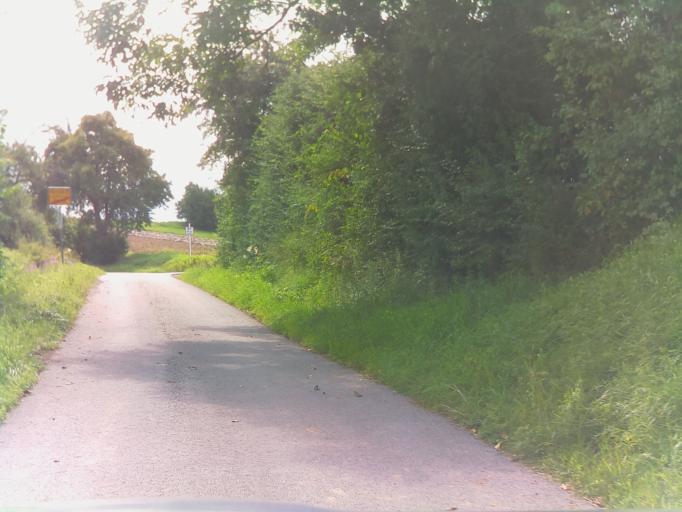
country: DE
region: Bavaria
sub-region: Upper Franconia
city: Grossheirath
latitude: 50.1372
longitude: 10.9498
